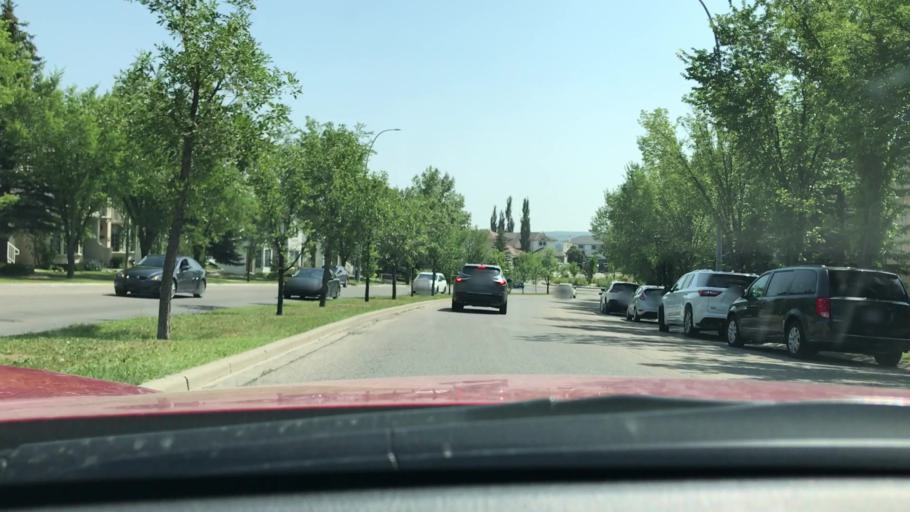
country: CA
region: Alberta
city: Calgary
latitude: 51.0218
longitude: -114.1842
